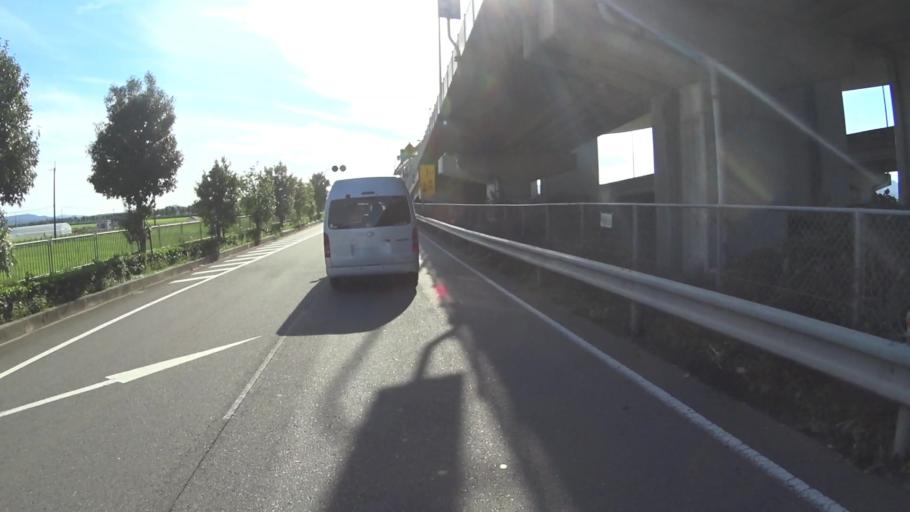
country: JP
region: Kyoto
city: Uji
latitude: 34.9041
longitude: 135.7663
